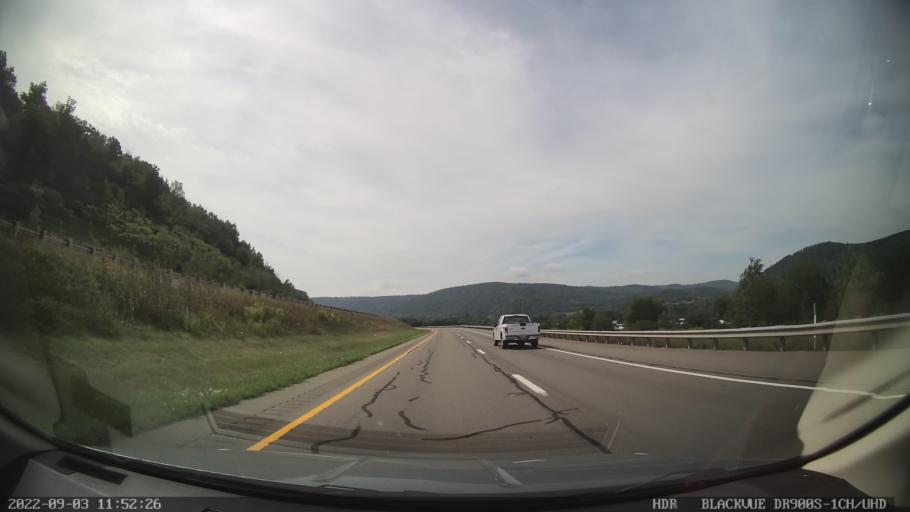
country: US
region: Pennsylvania
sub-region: Tioga County
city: Blossburg
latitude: 41.7366
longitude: -77.0727
